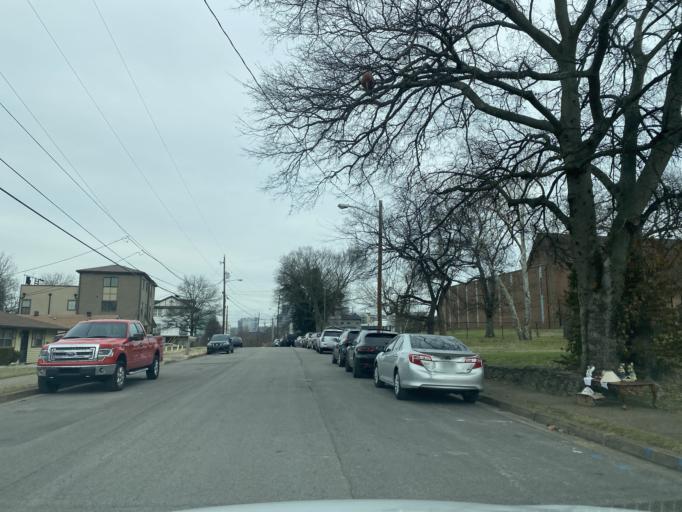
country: US
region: Tennessee
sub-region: Davidson County
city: Nashville
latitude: 36.1443
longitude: -86.7879
